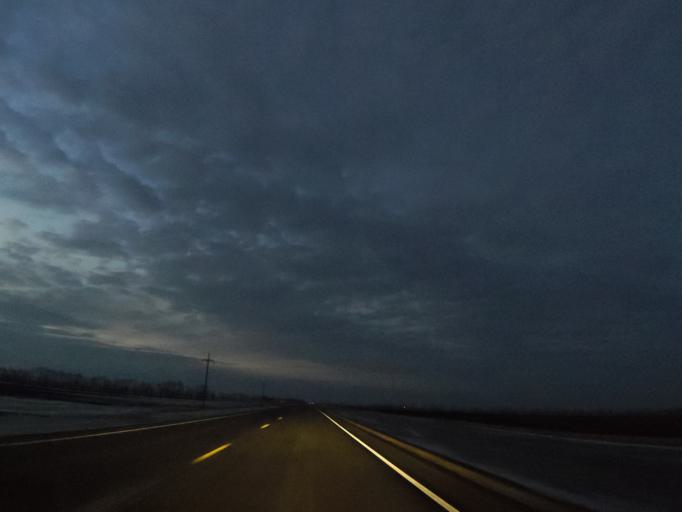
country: US
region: North Dakota
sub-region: Walsh County
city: Park River
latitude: 48.2971
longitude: -97.6224
